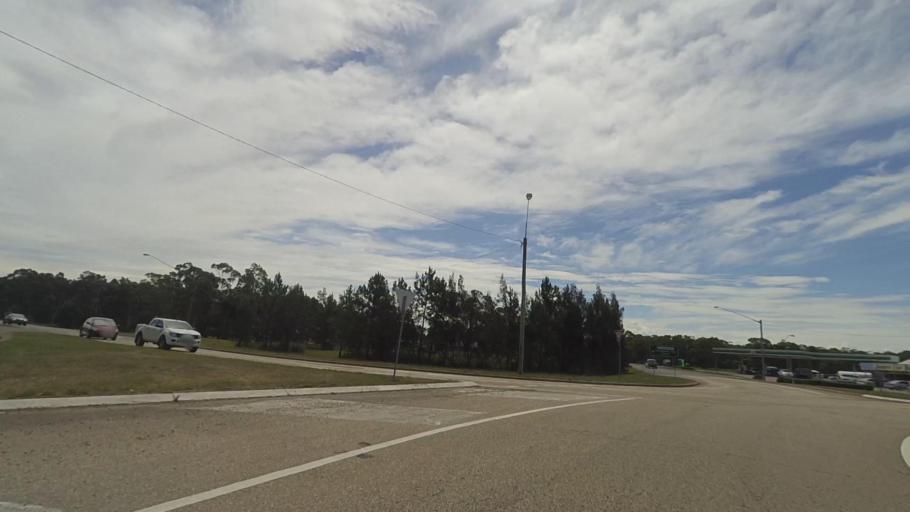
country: AU
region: New South Wales
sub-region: Port Stephens Shire
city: Medowie
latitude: -32.7895
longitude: 151.9030
